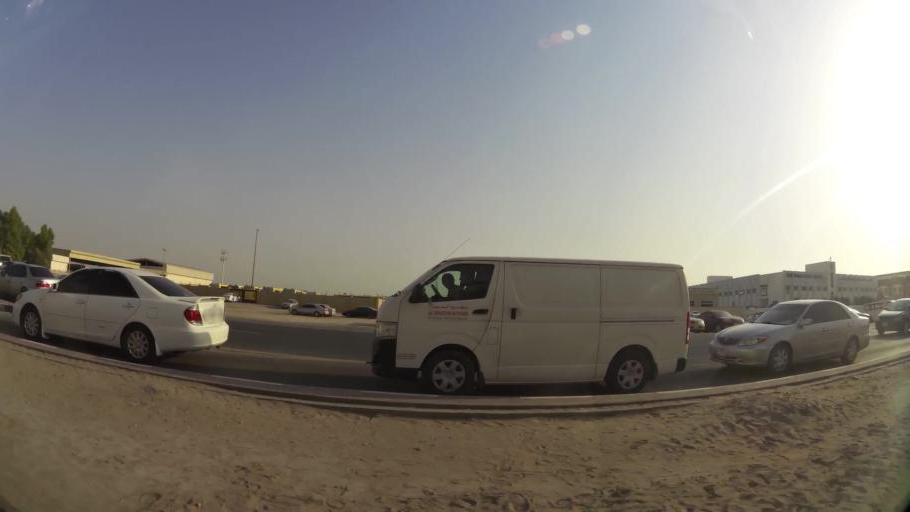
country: AE
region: Ajman
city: Ajman
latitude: 25.3800
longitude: 55.4507
